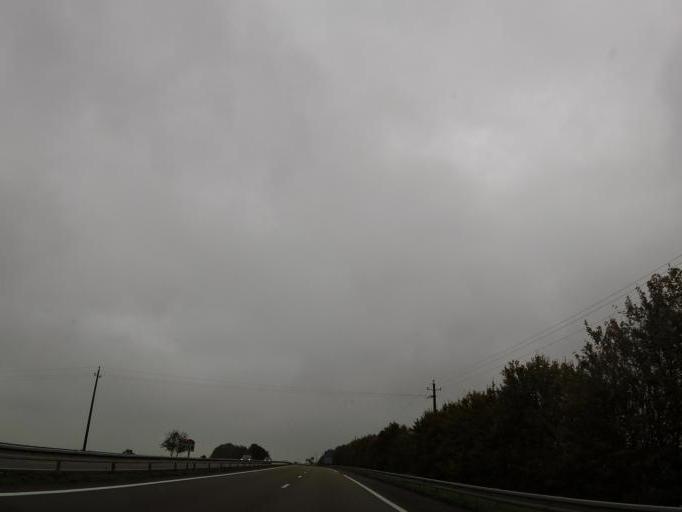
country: FR
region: Champagne-Ardenne
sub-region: Departement de la Marne
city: Verzy
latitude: 49.1308
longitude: 4.2252
